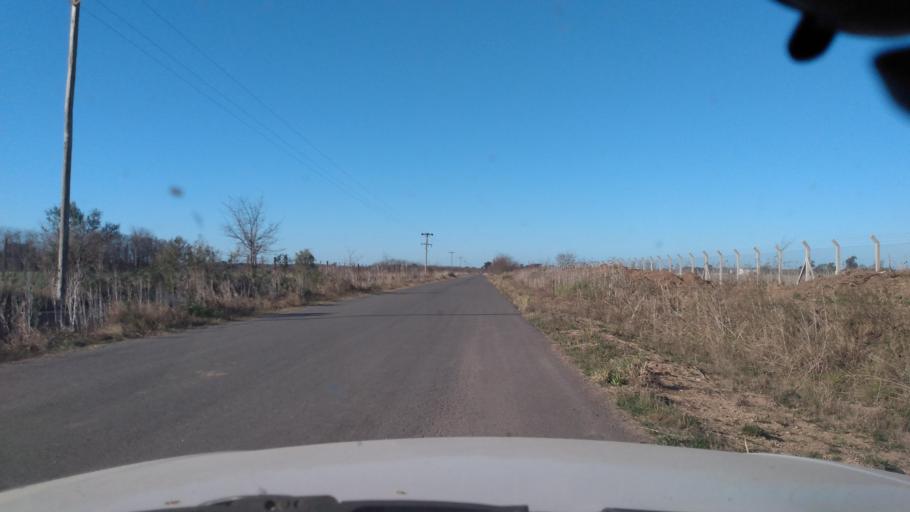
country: AR
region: Buenos Aires
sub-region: Partido de Mercedes
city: Mercedes
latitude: -34.6195
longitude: -59.3401
